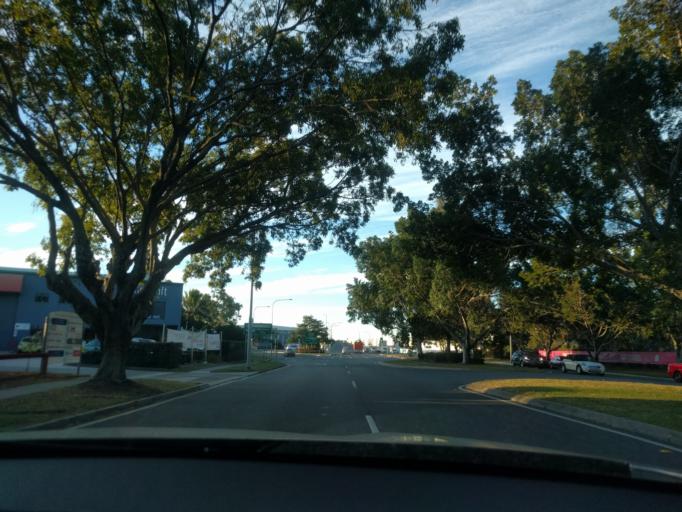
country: AU
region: Queensland
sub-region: Brisbane
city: Ascot
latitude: -27.4331
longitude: 153.0880
